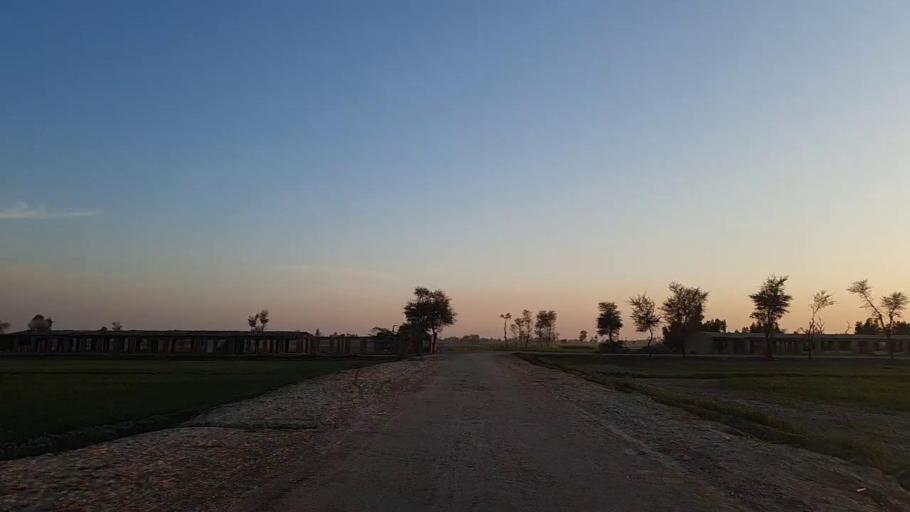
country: PK
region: Sindh
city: Bandhi
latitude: 26.6209
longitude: 68.3644
